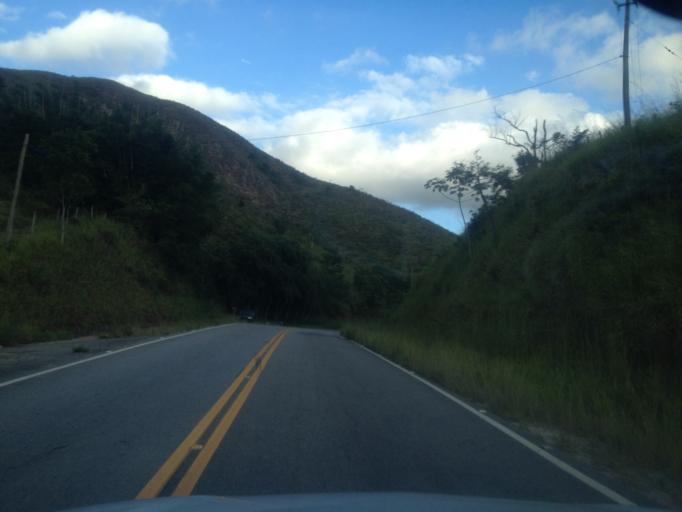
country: BR
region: Rio de Janeiro
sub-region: Quatis
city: Quatis
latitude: -22.3787
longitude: -44.2618
